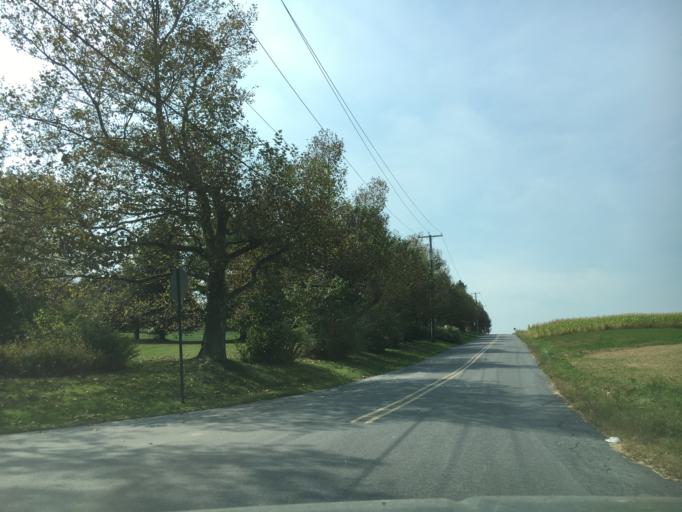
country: US
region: Pennsylvania
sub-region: Berks County
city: Topton
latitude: 40.5521
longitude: -75.7093
